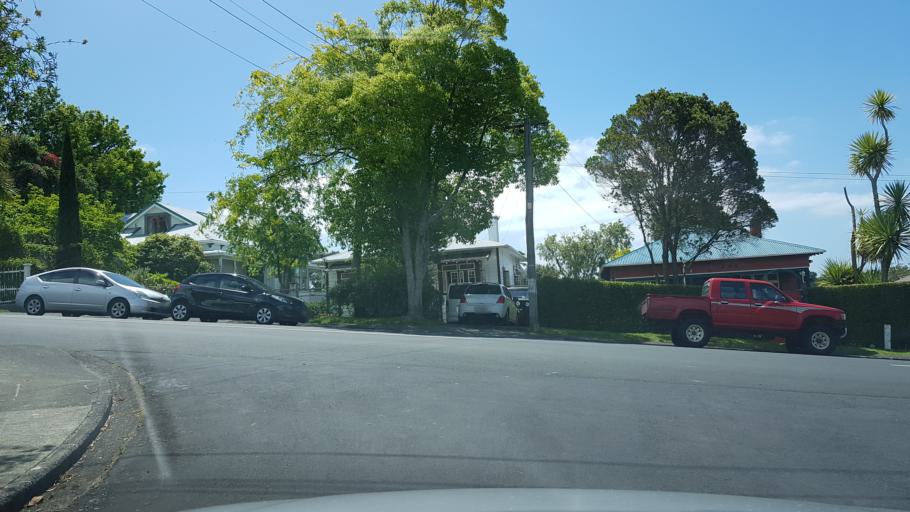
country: NZ
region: Auckland
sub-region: Auckland
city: North Shore
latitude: -36.8174
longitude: 174.7366
